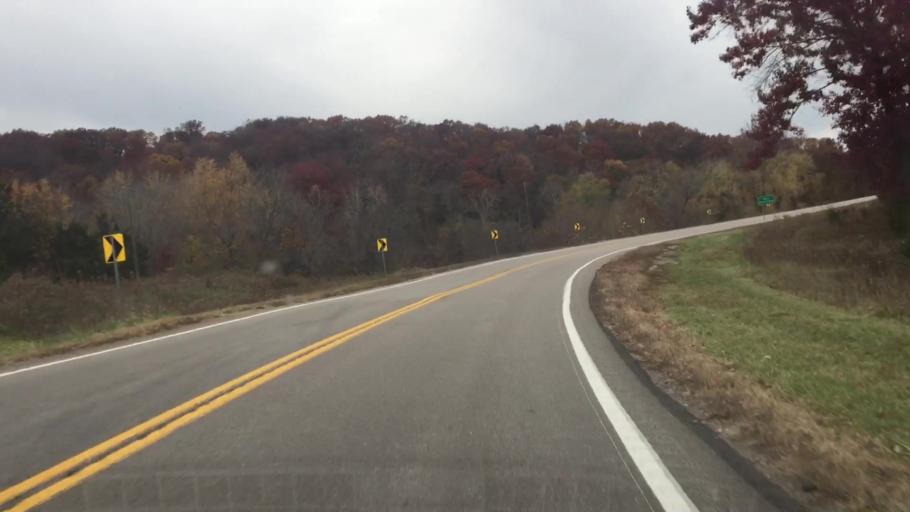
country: US
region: Missouri
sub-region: Gasconade County
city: Hermann
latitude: 38.7178
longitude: -91.6886
